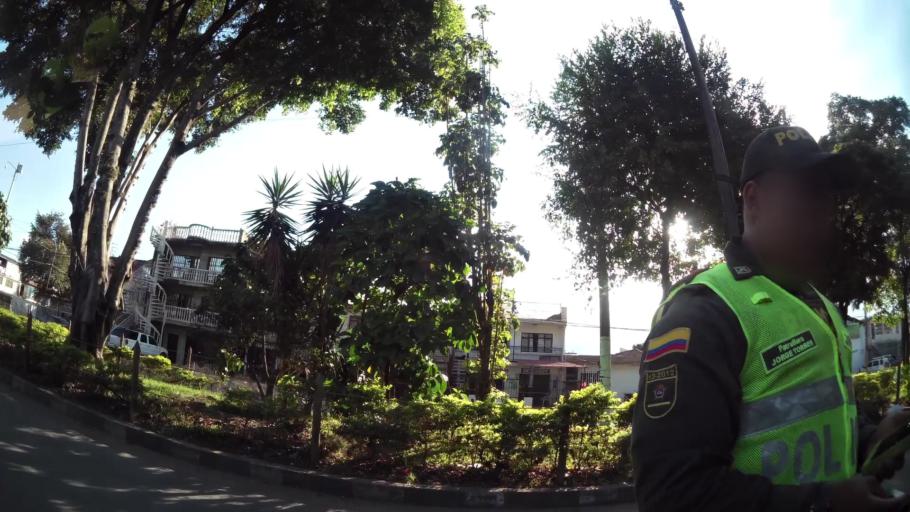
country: CO
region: Valle del Cauca
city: Cali
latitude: 3.4094
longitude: -76.5118
